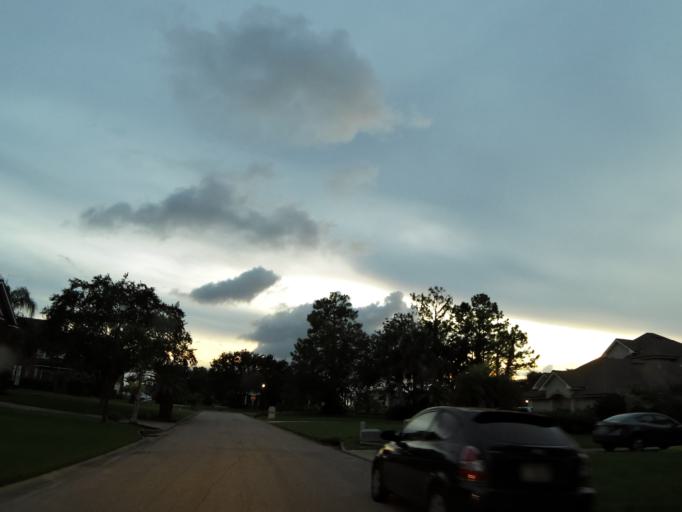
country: US
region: Florida
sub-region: Duval County
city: Jacksonville
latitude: 30.3849
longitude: -81.6209
